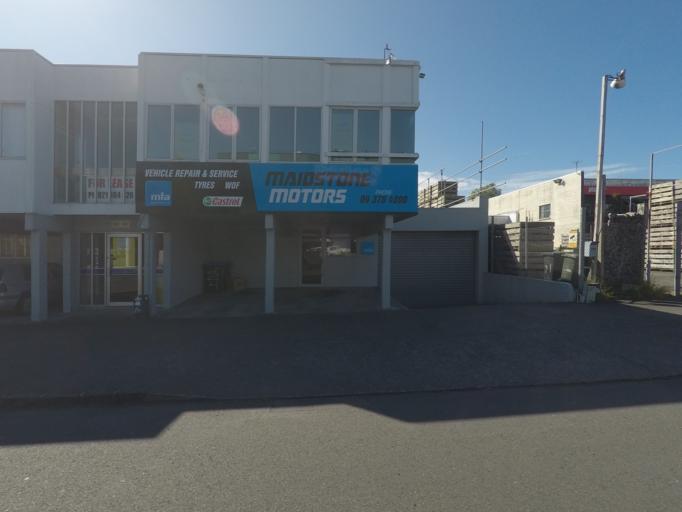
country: NZ
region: Auckland
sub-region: Auckland
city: Auckland
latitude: -36.8649
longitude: 174.7458
